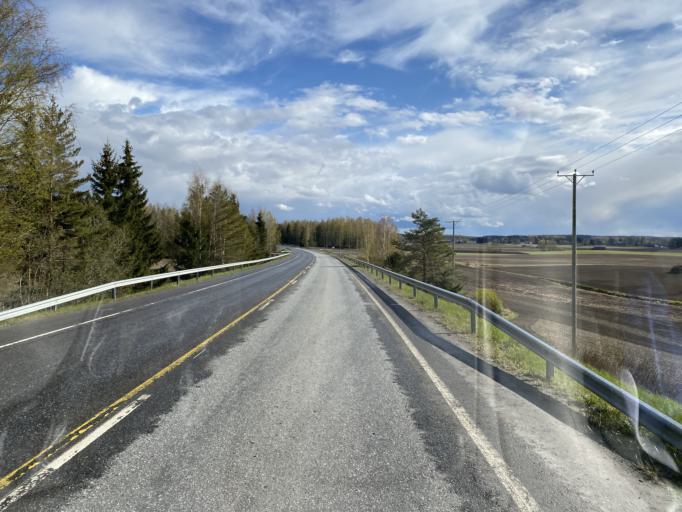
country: FI
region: Pirkanmaa
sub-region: Etelae-Pirkanmaa
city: Viiala
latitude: 61.2454
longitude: 23.7388
